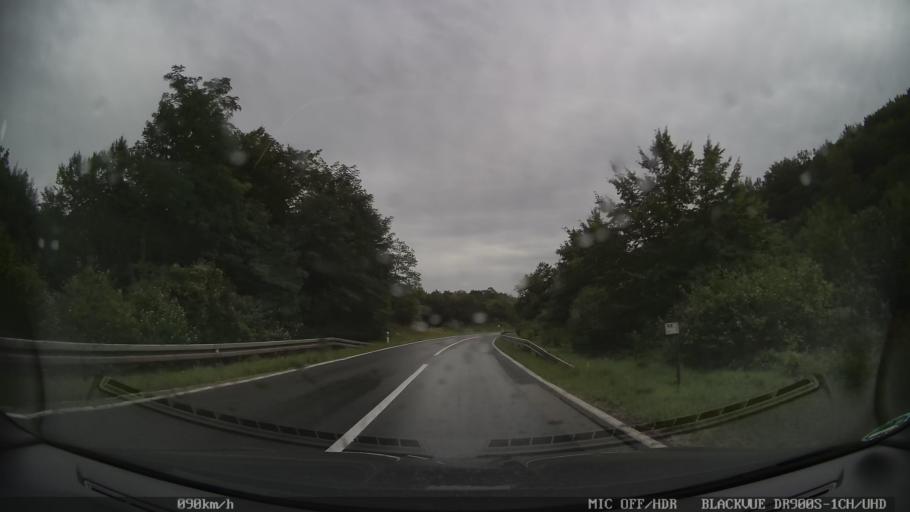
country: HR
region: Licko-Senjska
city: Brinje
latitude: 44.9620
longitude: 15.0870
